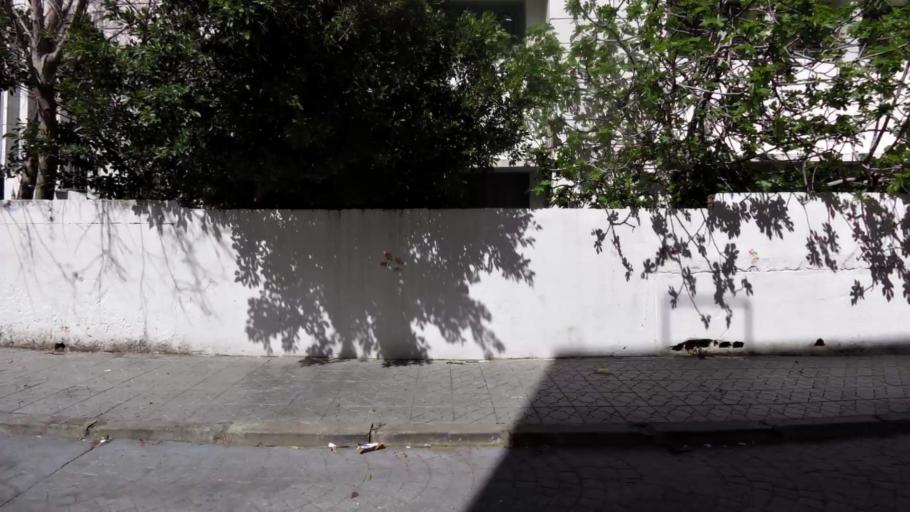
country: MA
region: Tanger-Tetouan
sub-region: Tanger-Assilah
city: Tangier
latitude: 35.7507
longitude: -5.8136
